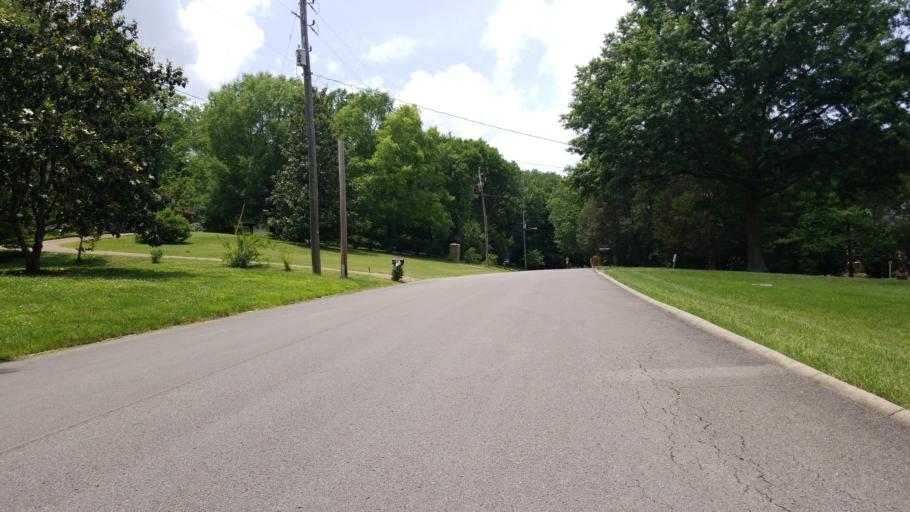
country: US
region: Tennessee
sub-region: Davidson County
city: Forest Hills
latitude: 36.0369
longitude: -86.8614
